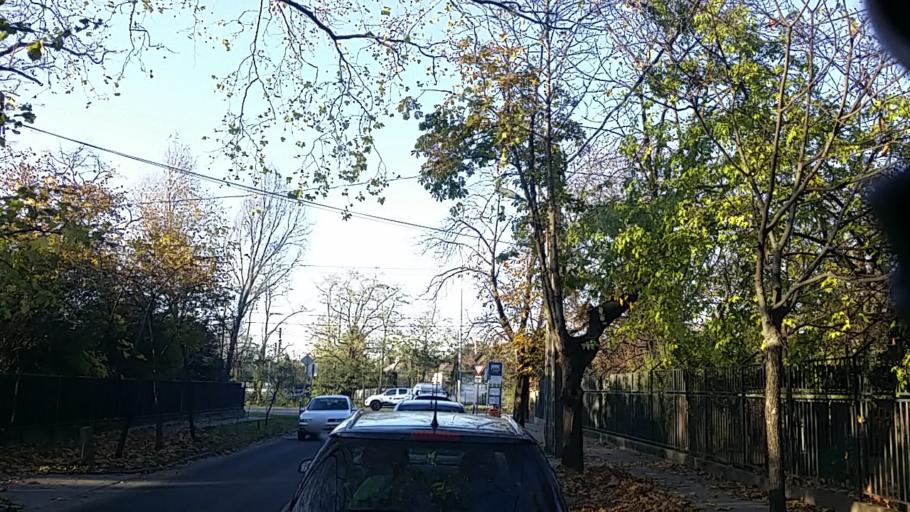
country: HU
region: Budapest
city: Budapest XVI. keruelet
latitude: 47.5138
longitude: 19.2031
